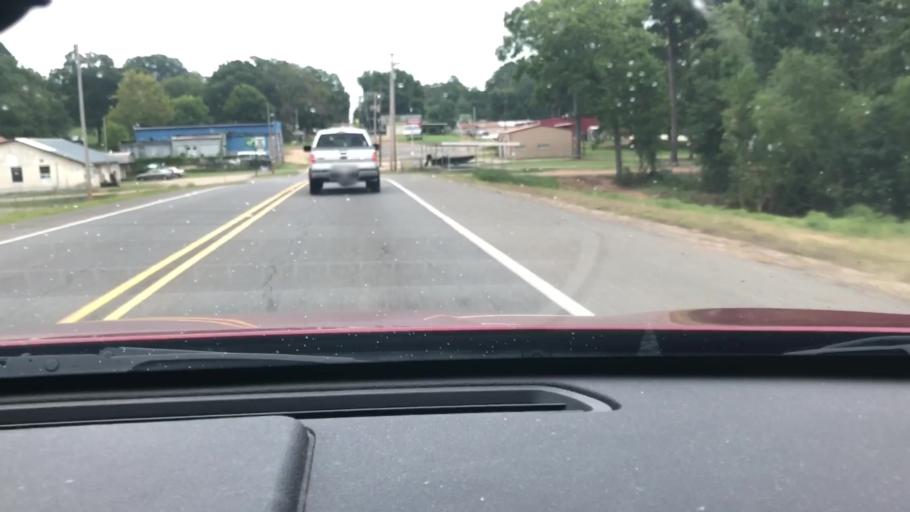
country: US
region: Arkansas
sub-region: Lafayette County
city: Stamps
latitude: 33.3657
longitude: -93.5001
